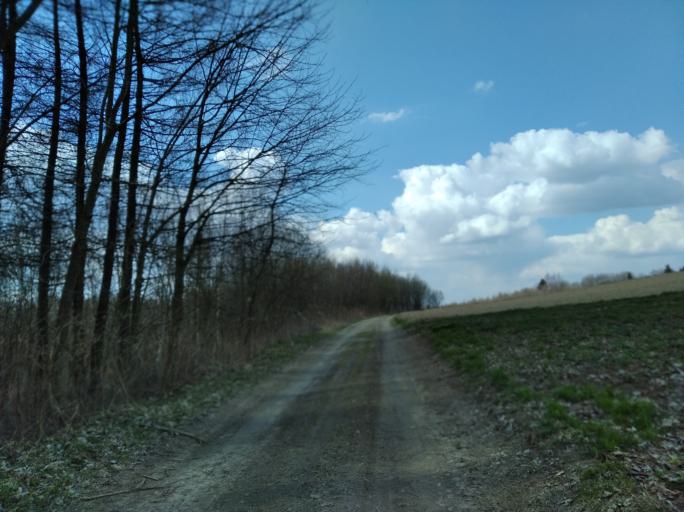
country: PL
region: Subcarpathian Voivodeship
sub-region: Powiat strzyzowski
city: Strzyzow
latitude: 49.9272
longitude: 21.7276
